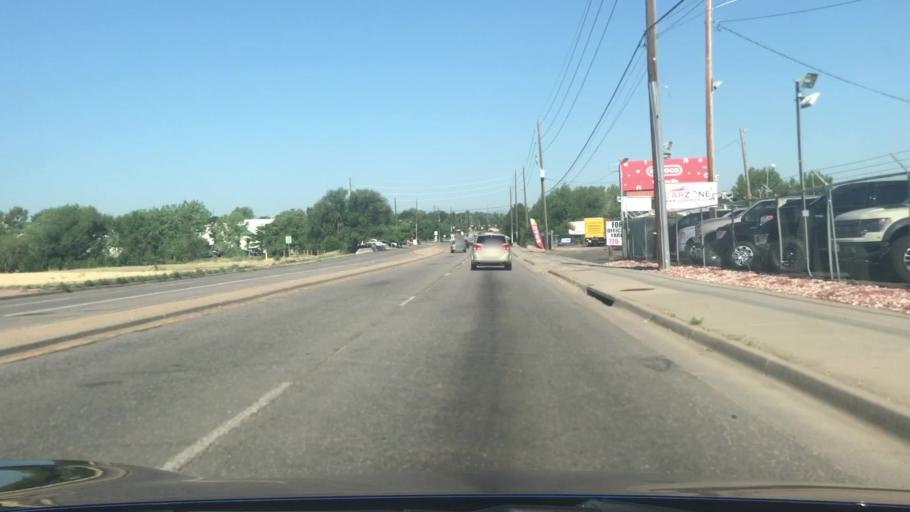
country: US
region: Colorado
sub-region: Arapahoe County
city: Glendale
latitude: 39.6749
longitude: -104.8920
